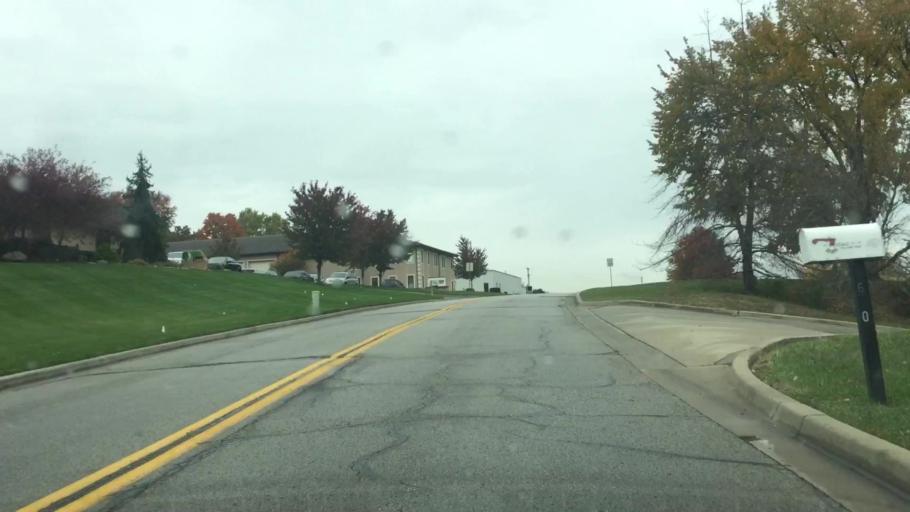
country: US
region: Kansas
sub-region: Wyandotte County
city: Edwardsville
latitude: 39.0025
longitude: -94.8246
